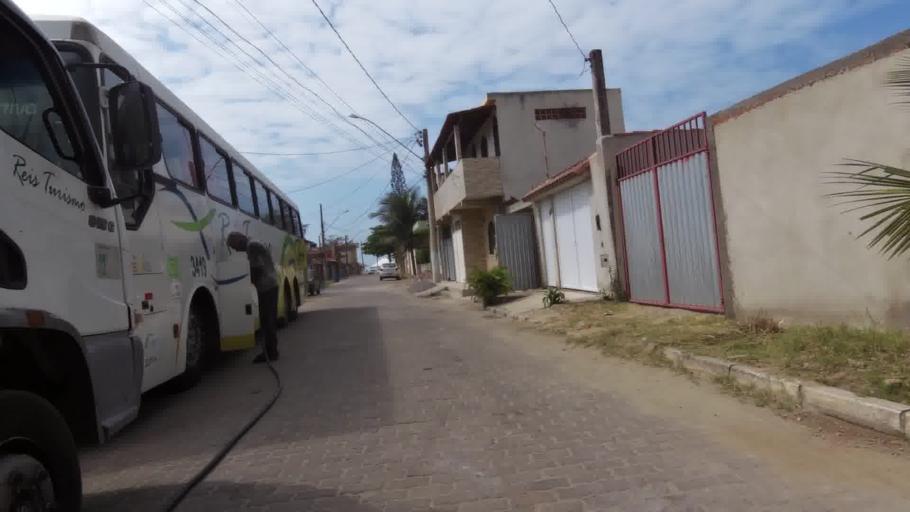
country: BR
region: Espirito Santo
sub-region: Marataizes
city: Marataizes
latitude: -21.0274
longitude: -40.8136
